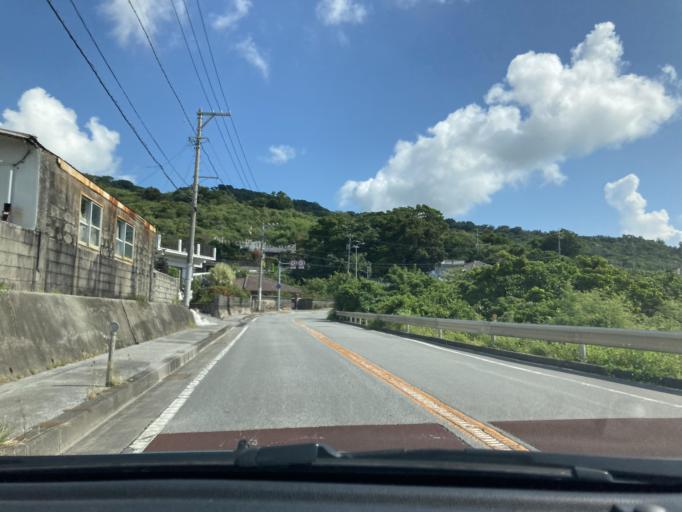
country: JP
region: Okinawa
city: Tomigusuku
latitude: 26.1391
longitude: 127.7770
